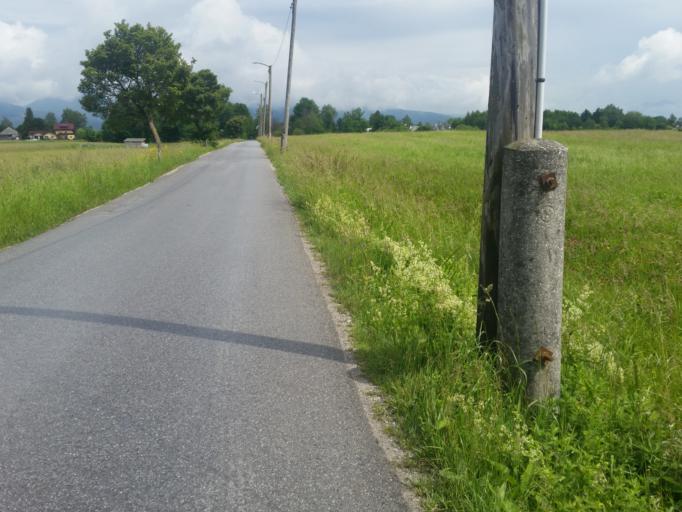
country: AT
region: Salzburg
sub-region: Salzburg Stadt
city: Salzburg
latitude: 47.7770
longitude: 13.0151
